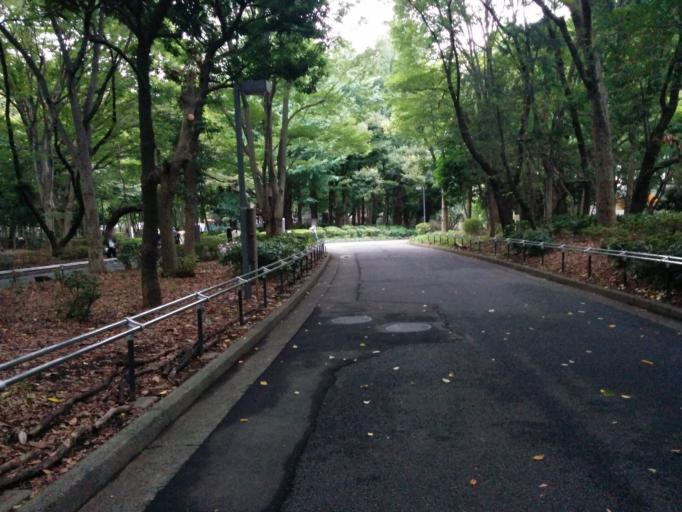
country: JP
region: Tokyo
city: Tokyo
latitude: 35.6897
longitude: 139.6892
